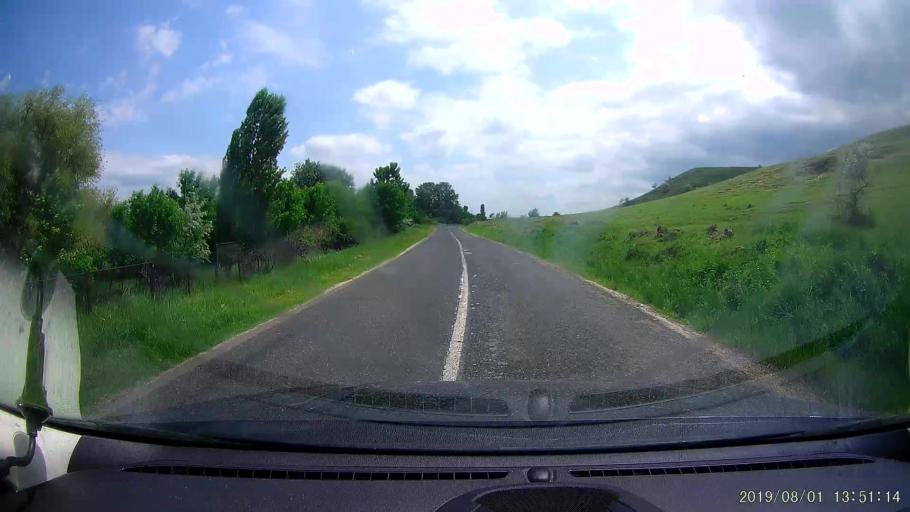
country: RO
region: Galati
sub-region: Comuna Vladesti
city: Vladesti
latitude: 45.8690
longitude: 28.0961
